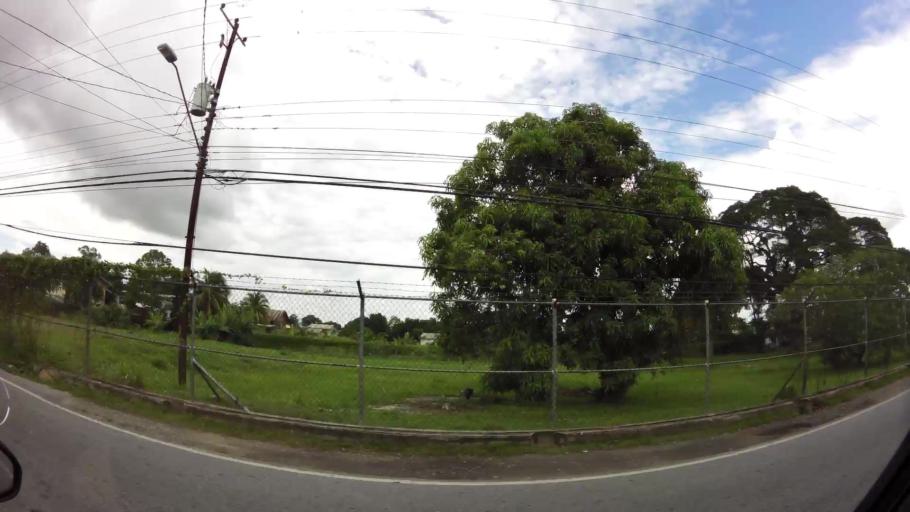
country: TT
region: Chaguanas
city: Chaguanas
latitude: 10.4845
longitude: -61.4080
